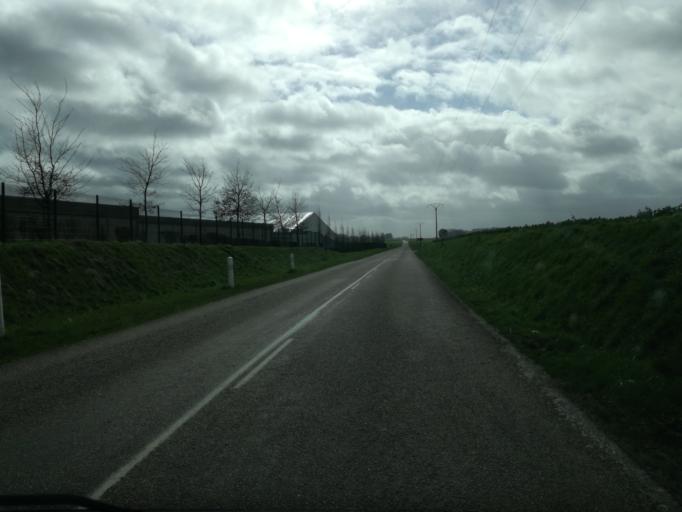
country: FR
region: Haute-Normandie
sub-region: Departement de la Seine-Maritime
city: Valliquerville
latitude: 49.6095
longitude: 0.6659
